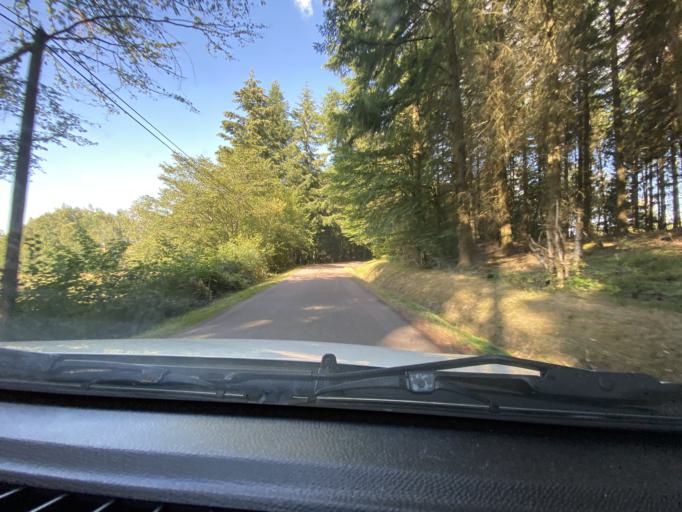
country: FR
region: Bourgogne
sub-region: Departement de la Cote-d'Or
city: Saulieu
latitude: 47.3110
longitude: 4.1945
